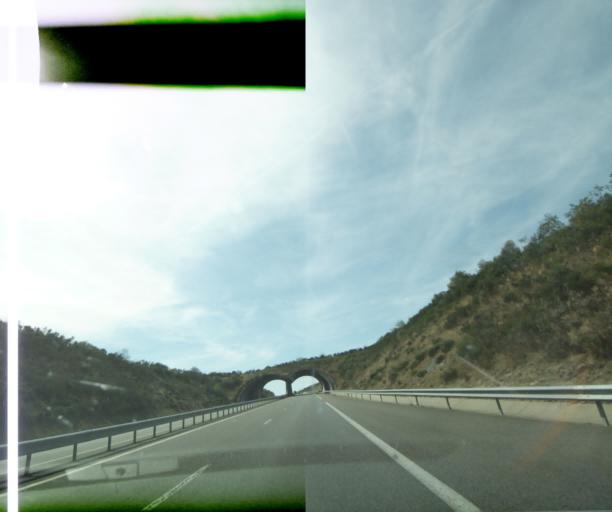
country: FR
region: Auvergne
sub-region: Departement du Puy-de-Dome
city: Charbonnieres-les-Varennes
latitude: 45.9045
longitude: 2.9461
